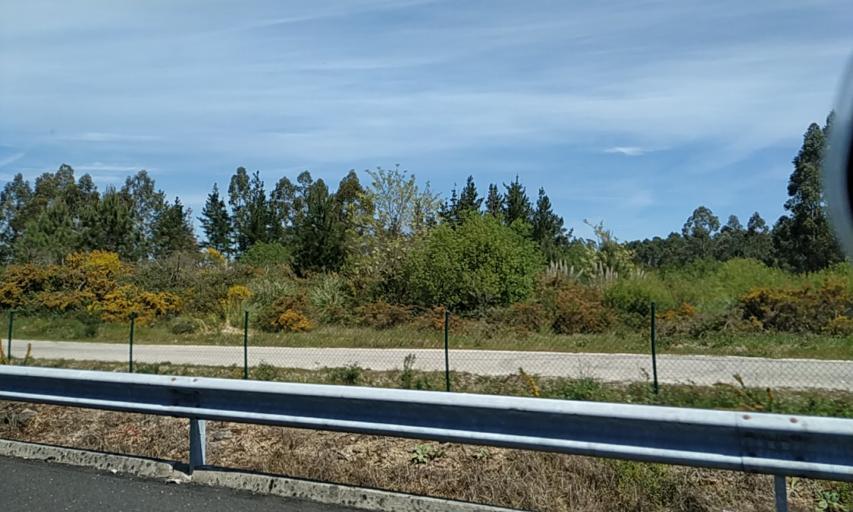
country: ES
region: Galicia
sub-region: Provincia de Pontevedra
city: Portas
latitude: 42.5574
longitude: -8.6722
